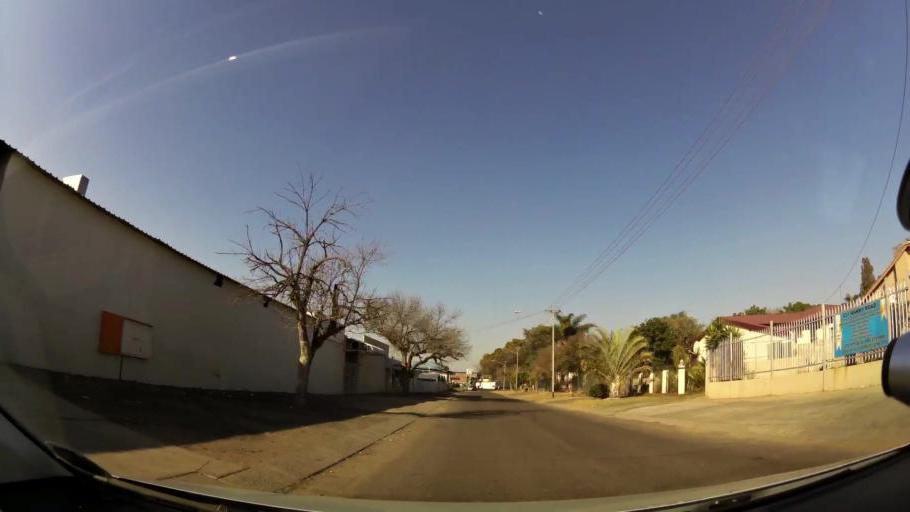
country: ZA
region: Gauteng
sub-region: City of Tshwane Metropolitan Municipality
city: Pretoria
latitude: -25.7233
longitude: 28.1583
